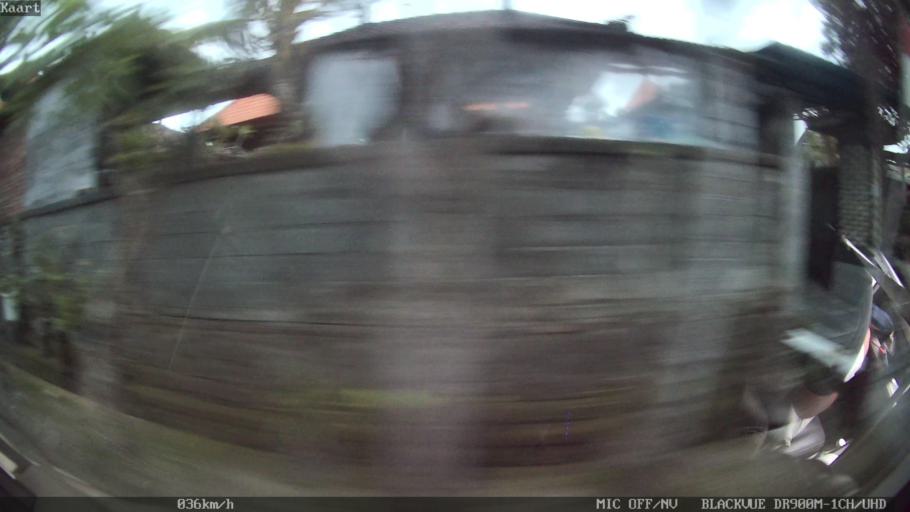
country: ID
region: Bali
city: Banjar Pasekan
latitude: -8.6291
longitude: 115.2867
